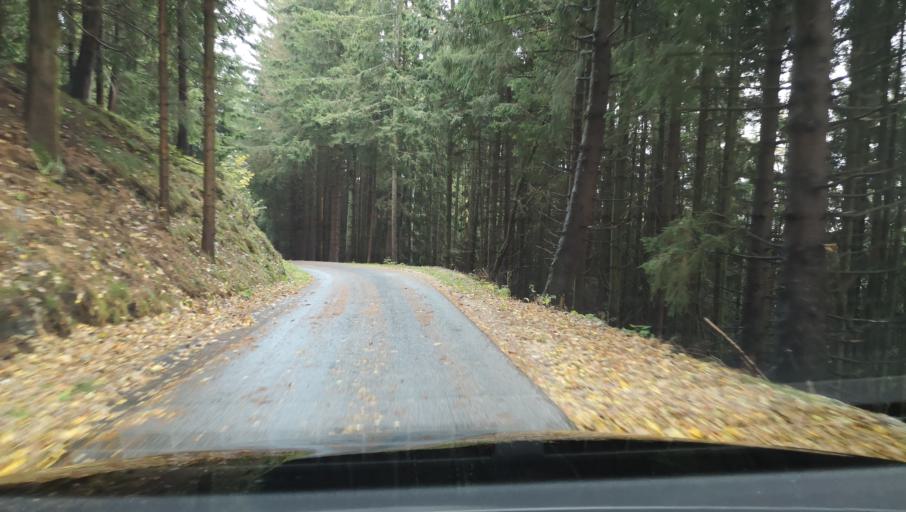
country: AT
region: Styria
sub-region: Politischer Bezirk Weiz
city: Gasen
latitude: 47.3588
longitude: 15.5953
